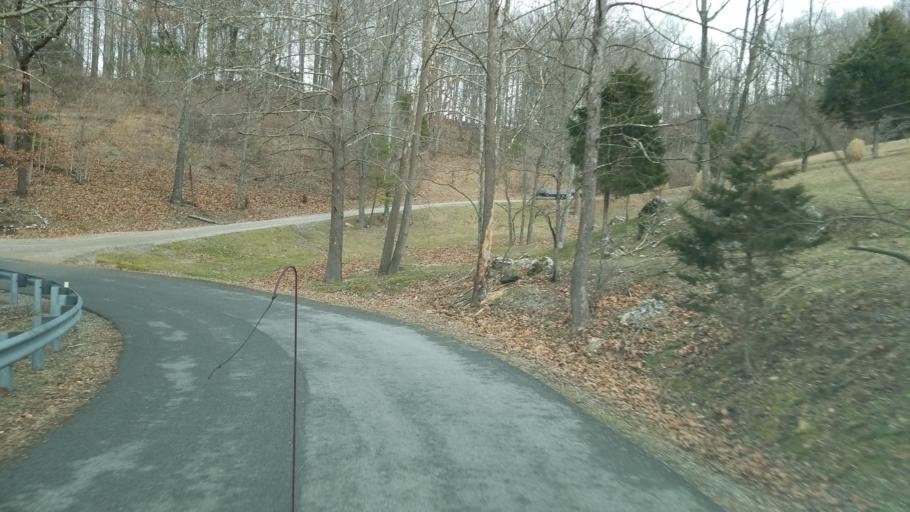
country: US
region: Virginia
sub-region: Giles County
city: Pearisburg
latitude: 37.2174
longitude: -80.7070
